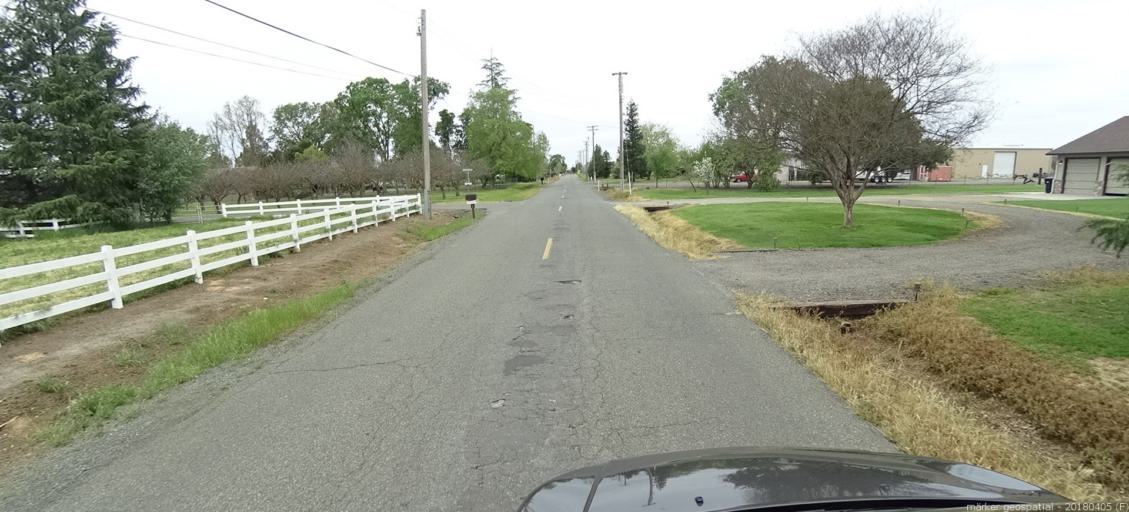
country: US
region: California
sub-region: Sacramento County
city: Galt
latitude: 38.2565
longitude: -121.3261
